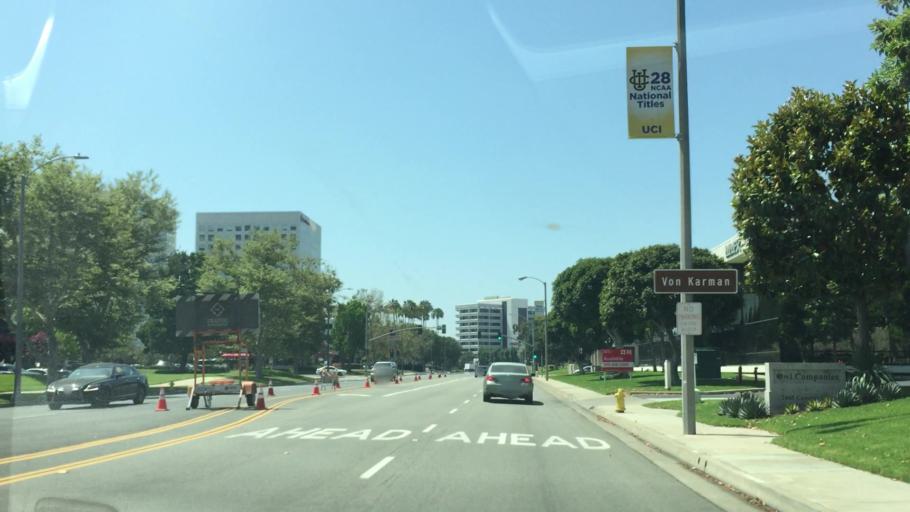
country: US
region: California
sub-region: Orange County
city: Irvine
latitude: 33.6689
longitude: -117.8581
